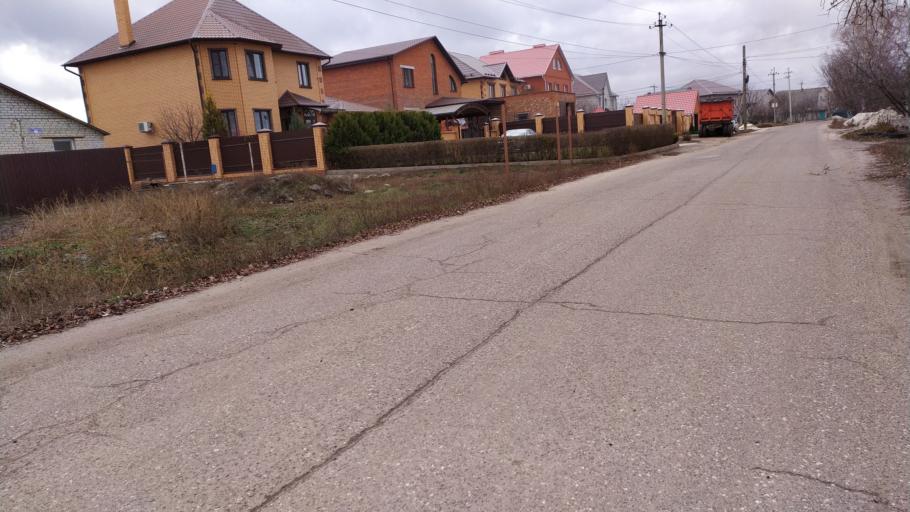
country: RU
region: Kursk
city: Kursk
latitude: 51.6384
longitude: 36.1424
